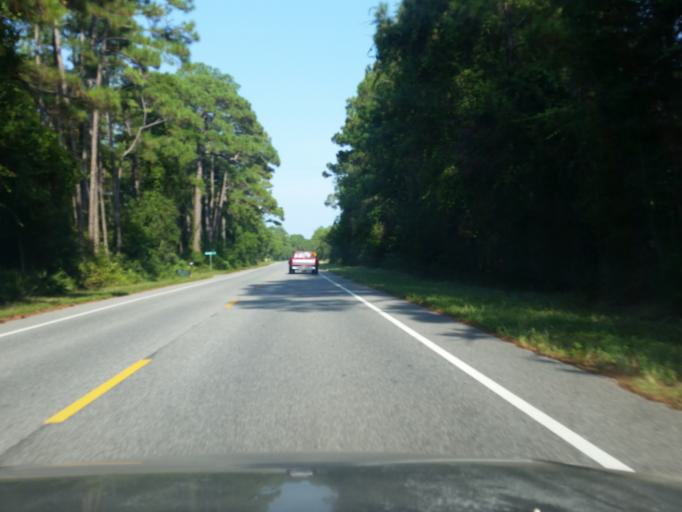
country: US
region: Alabama
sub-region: Baldwin County
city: Gulf Shores
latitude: 30.2492
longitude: -87.7952
